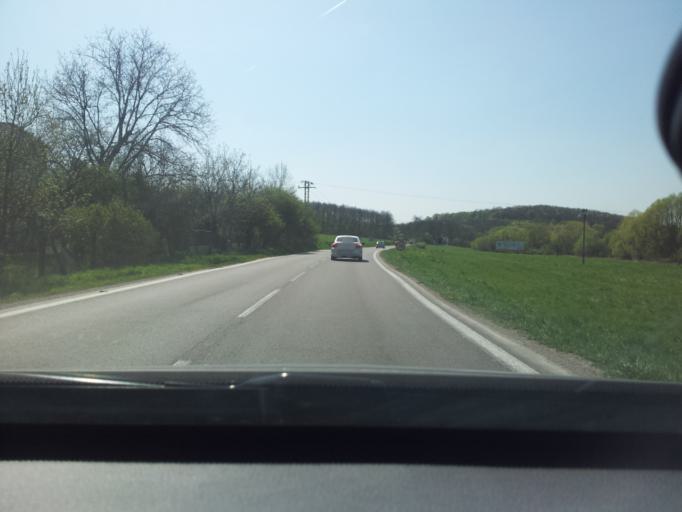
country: SK
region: Nitriansky
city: Banovce nad Bebravou
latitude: 48.7797
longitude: 18.1786
